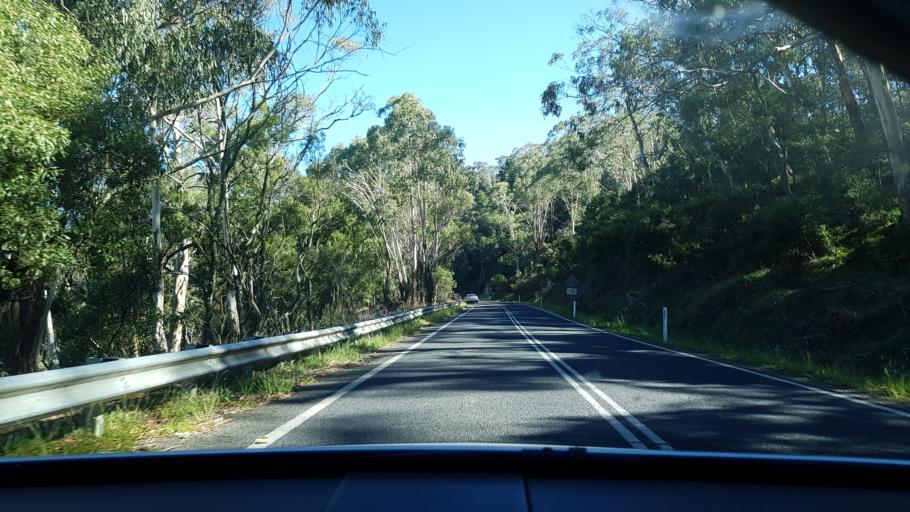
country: AU
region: New South Wales
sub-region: Lithgow
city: Bowenfels
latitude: -33.6642
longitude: 150.0505
